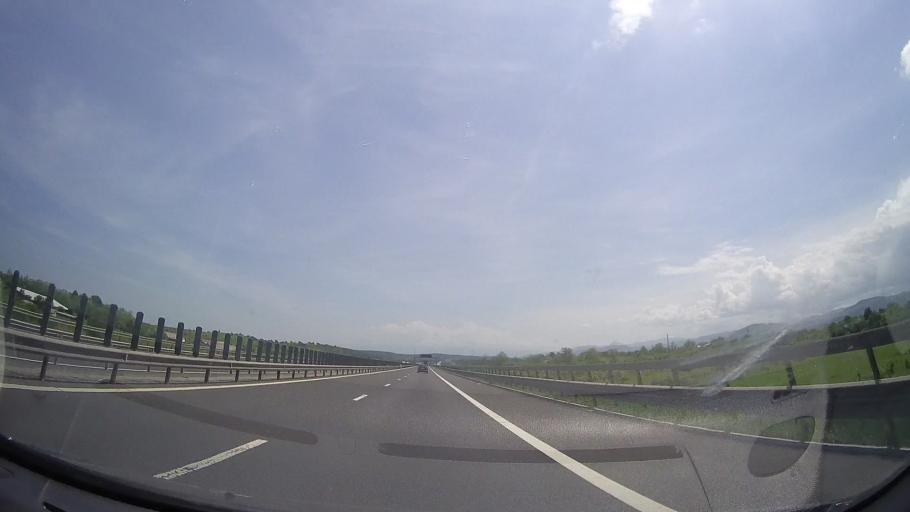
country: RO
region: Sibiu
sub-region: Oras Saliste
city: Saliste
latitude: 45.8124
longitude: 23.8904
